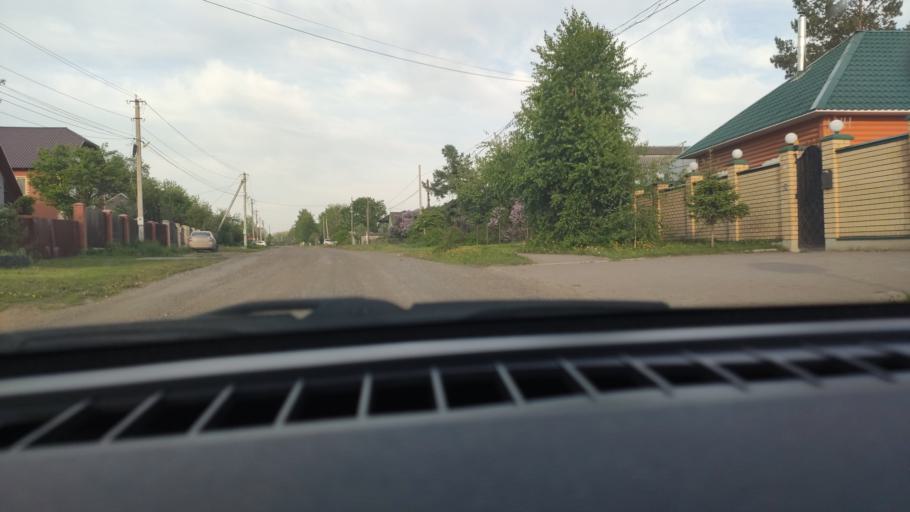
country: RU
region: Perm
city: Kondratovo
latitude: 57.9379
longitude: 56.0332
